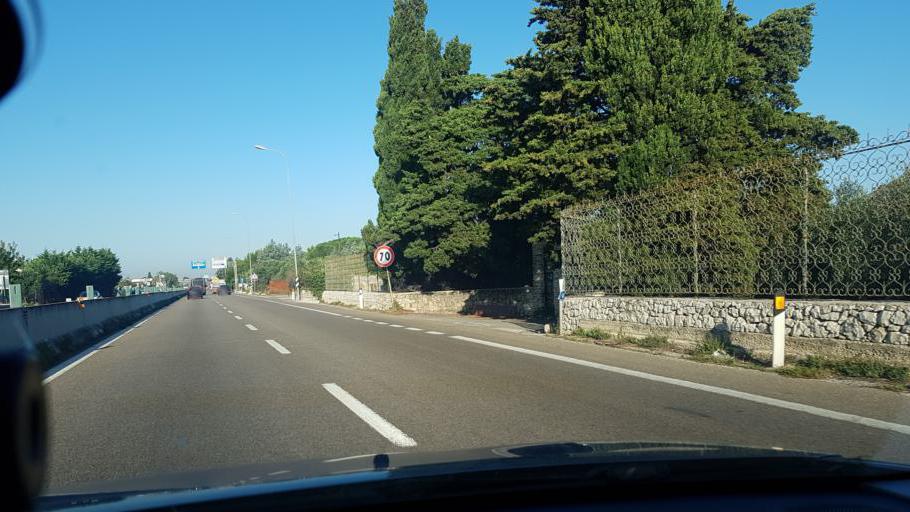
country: IT
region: Apulia
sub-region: Provincia di Bari
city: Parco Scizzo-Parchitello
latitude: 41.0906
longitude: 16.9717
